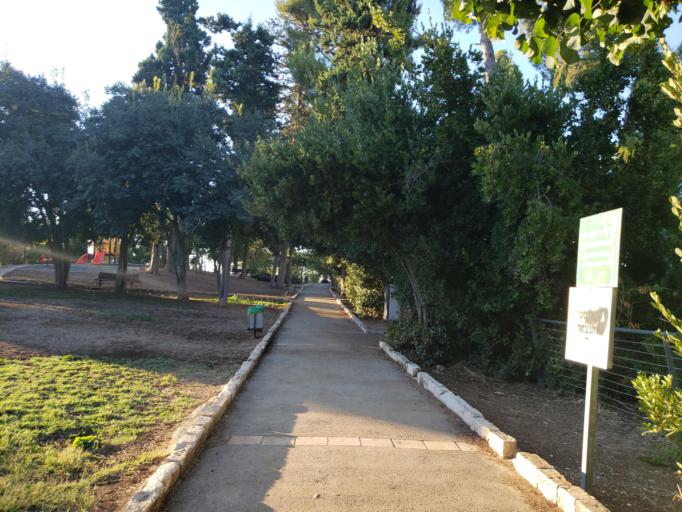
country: IL
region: Northern District
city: Safed
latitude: 32.9687
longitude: 35.4950
